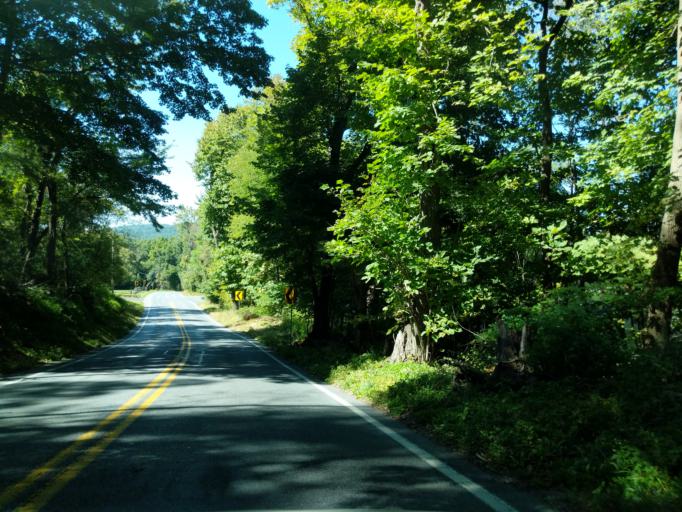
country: US
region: Pennsylvania
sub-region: Montgomery County
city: East Greenville
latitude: 40.4497
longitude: -75.4909
